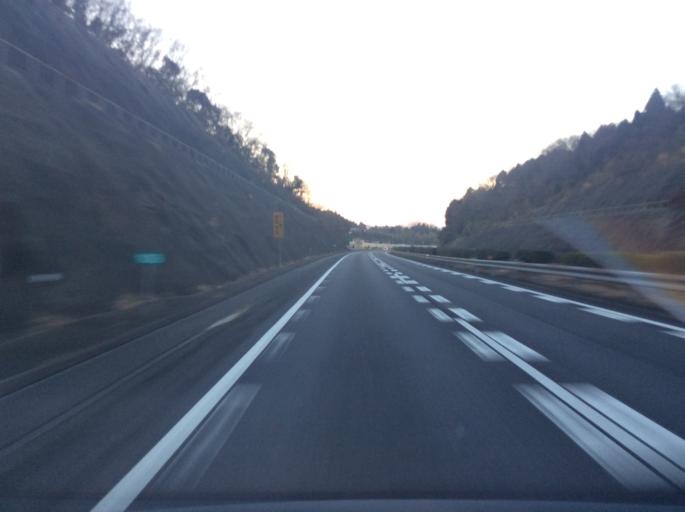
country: JP
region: Ibaraki
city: Funaishikawa
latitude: 36.5290
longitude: 140.5913
